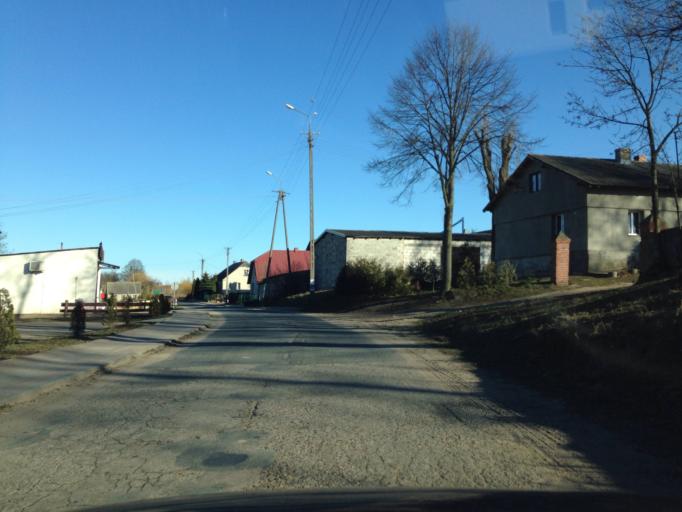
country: PL
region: Kujawsko-Pomorskie
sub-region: Powiat brodnicki
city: Brzozie
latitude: 53.3530
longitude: 19.6397
